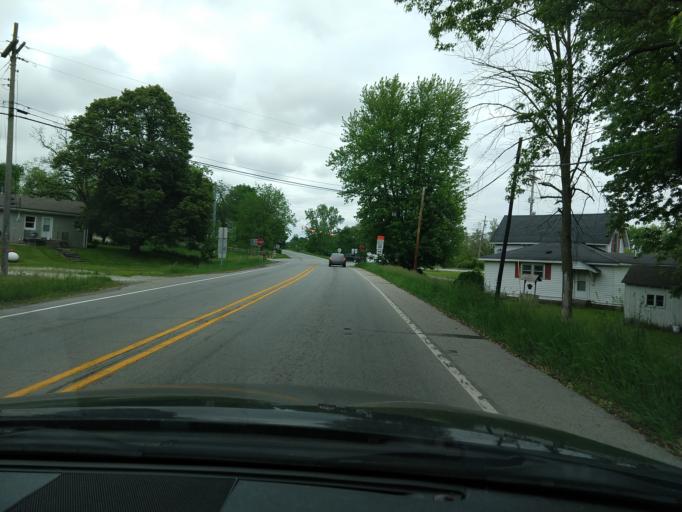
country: US
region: Indiana
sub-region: Madison County
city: Lapel
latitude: 40.0712
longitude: -85.8586
